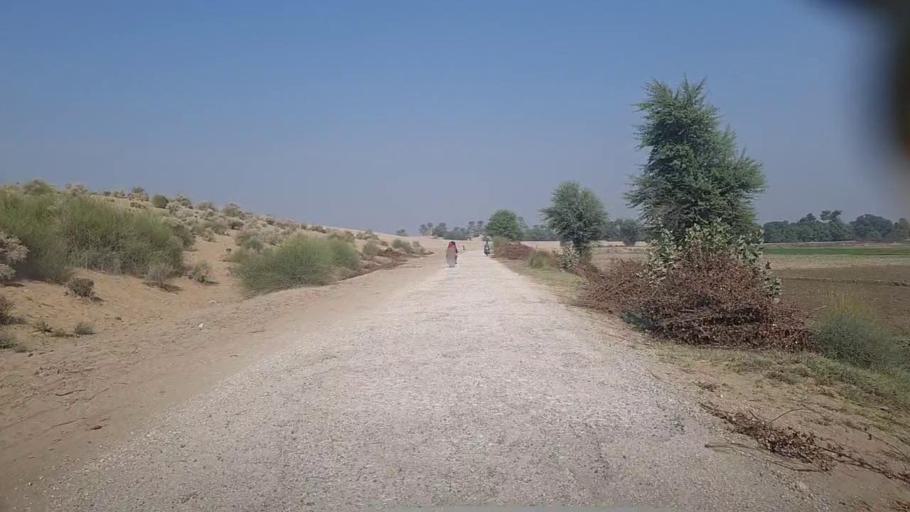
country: PK
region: Sindh
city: Kandiari
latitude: 26.9259
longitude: 68.5191
